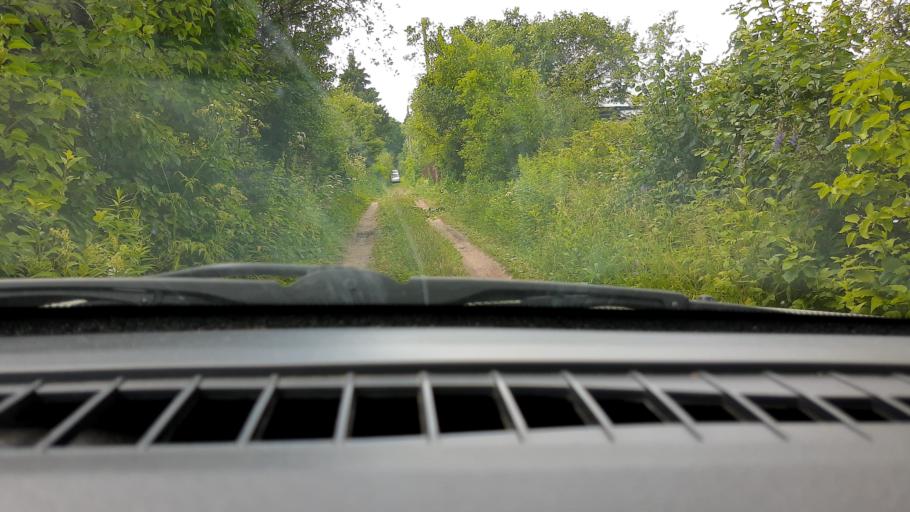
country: RU
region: Nizjnij Novgorod
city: Afonino
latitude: 56.2375
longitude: 44.0253
